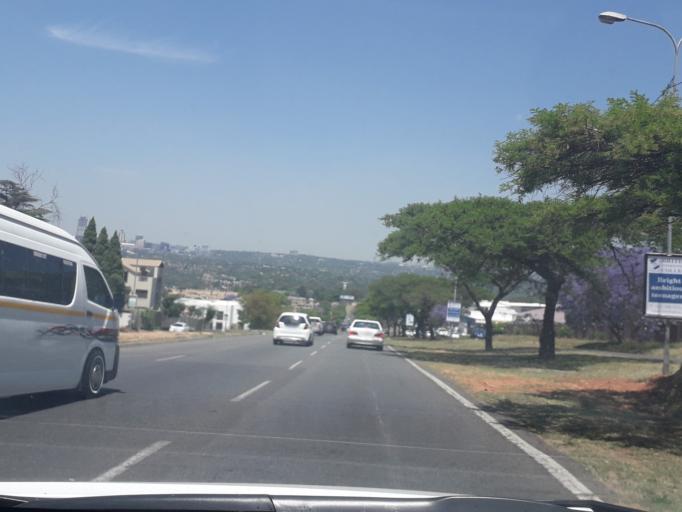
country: ZA
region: Gauteng
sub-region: City of Johannesburg Metropolitan Municipality
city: Midrand
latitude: -26.0649
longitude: 28.0247
